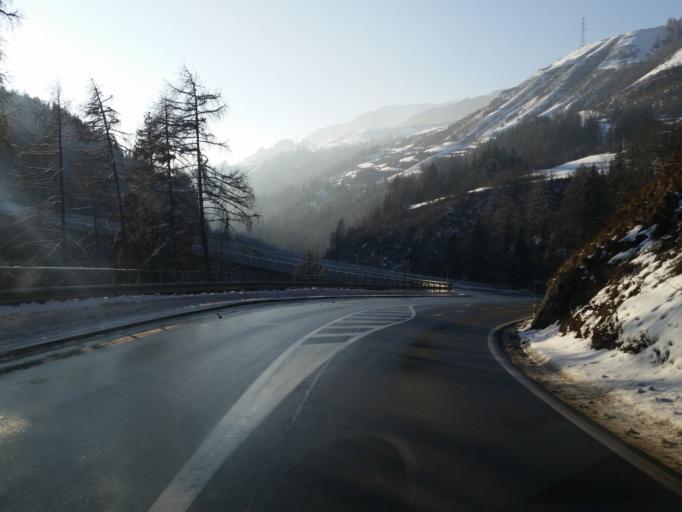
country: CH
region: Grisons
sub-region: Inn District
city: Scuol
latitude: 46.7899
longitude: 10.2843
